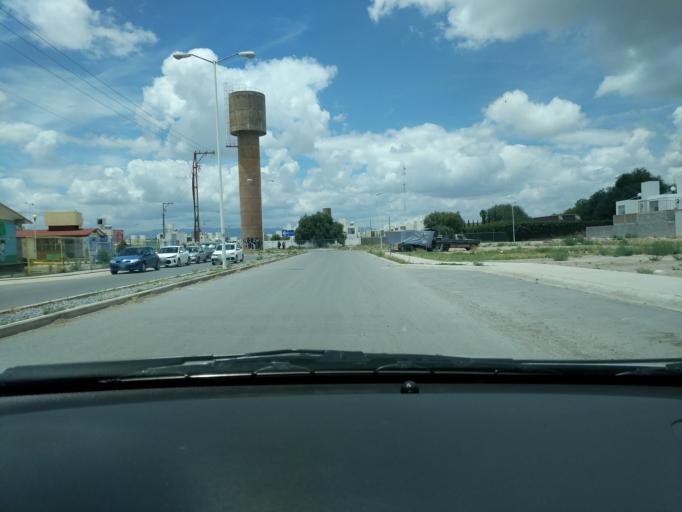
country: MX
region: San Luis Potosi
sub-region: San Luis Potosi
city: Fraccion Milpillas
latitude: 22.2199
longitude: -100.9349
